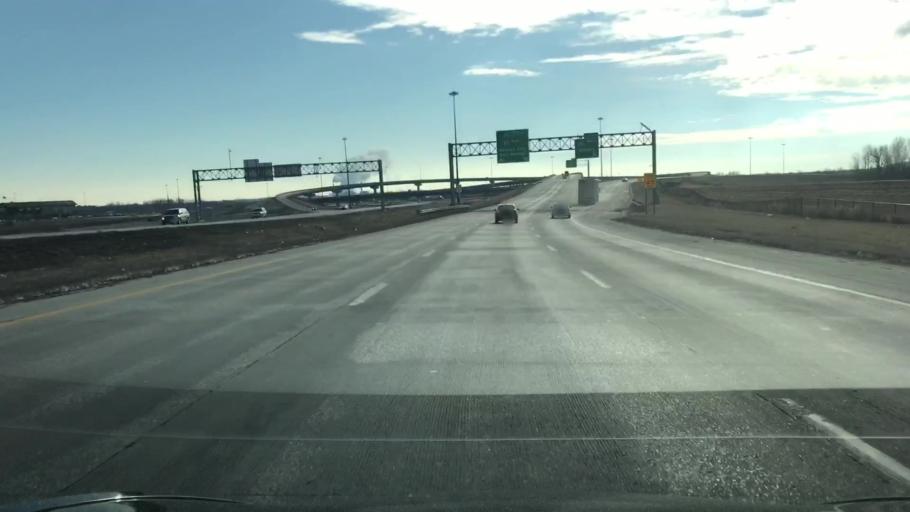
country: US
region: Nebraska
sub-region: Douglas County
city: Omaha
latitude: 41.2394
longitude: -95.9025
